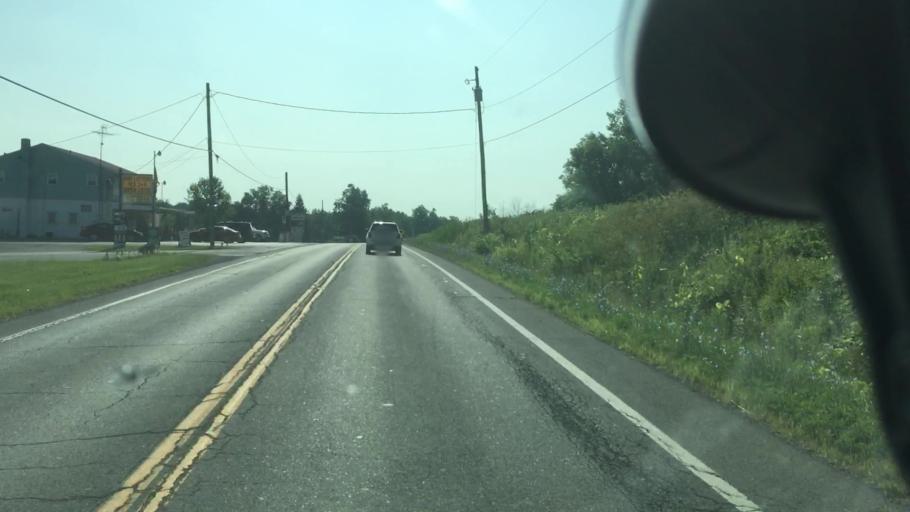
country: US
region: Ohio
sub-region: Mahoning County
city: Lowellville
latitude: 41.0241
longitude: -80.5230
